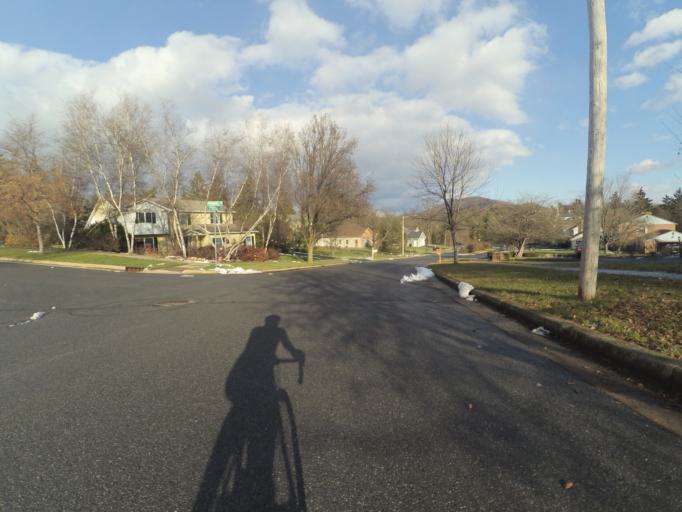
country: US
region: Pennsylvania
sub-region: Centre County
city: Lemont
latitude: 40.7922
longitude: -77.8345
